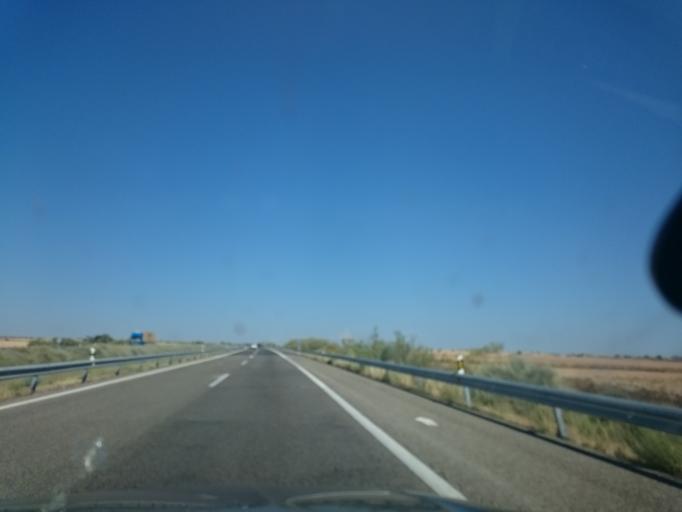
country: ES
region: Aragon
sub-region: Provincia de Zaragoza
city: Mequinensa / Mequinenza
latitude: 41.4681
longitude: 0.2303
